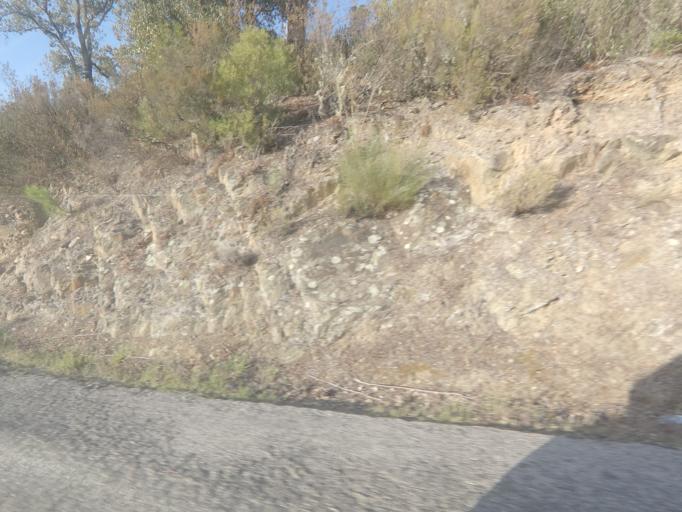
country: PT
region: Viseu
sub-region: Armamar
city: Armamar
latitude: 41.1309
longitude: -7.6774
